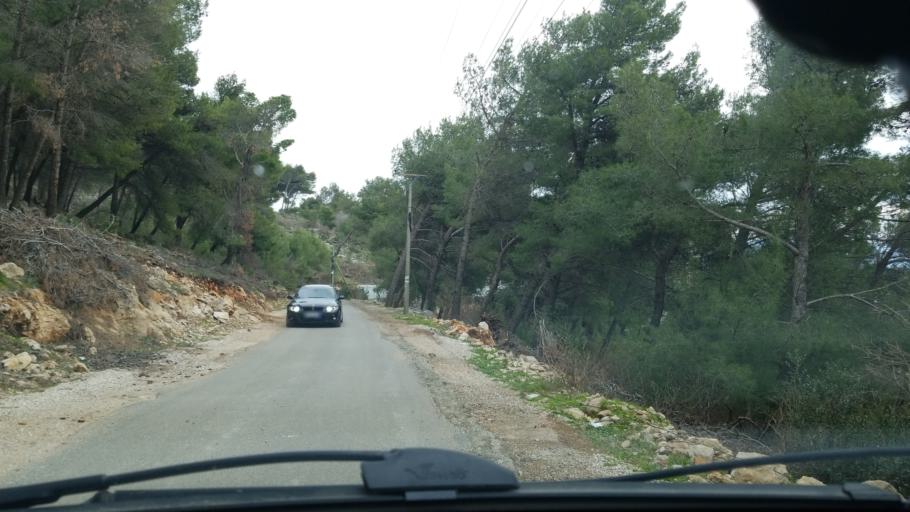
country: AL
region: Lezhe
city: Shengjin
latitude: 41.8146
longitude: 19.5715
